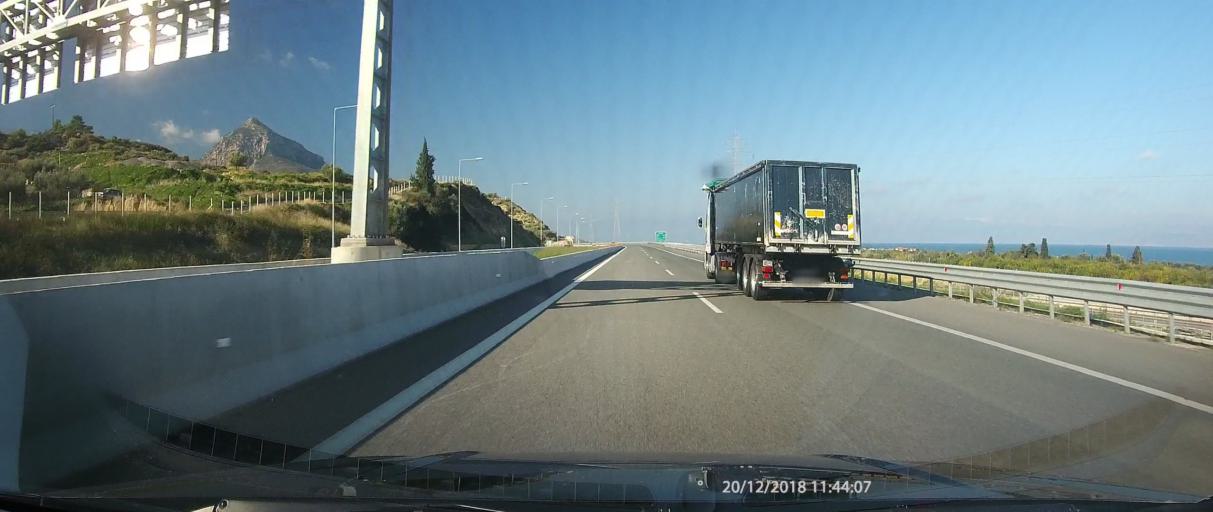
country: GR
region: Peloponnese
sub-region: Nomos Korinthias
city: Xylokastro
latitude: 38.0760
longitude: 22.6086
